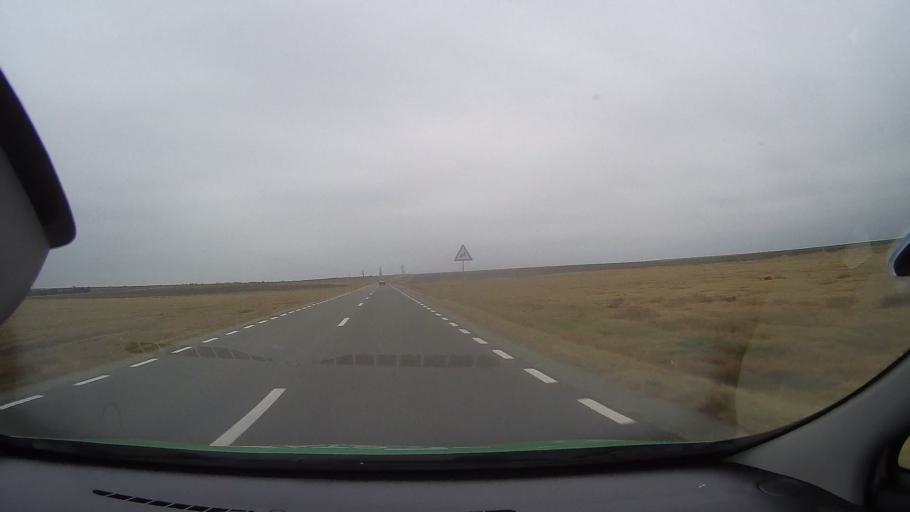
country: RO
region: Ialomita
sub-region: Comuna Scanteia
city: Iazu
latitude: 44.7231
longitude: 27.4224
